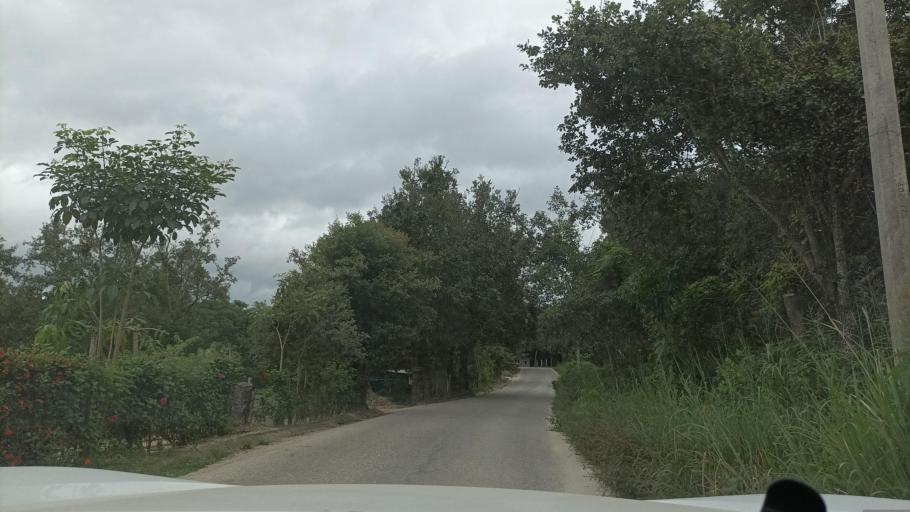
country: MX
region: Veracruz
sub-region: Cosoleacaque
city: Coacotla
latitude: 17.9465
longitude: -94.7080
